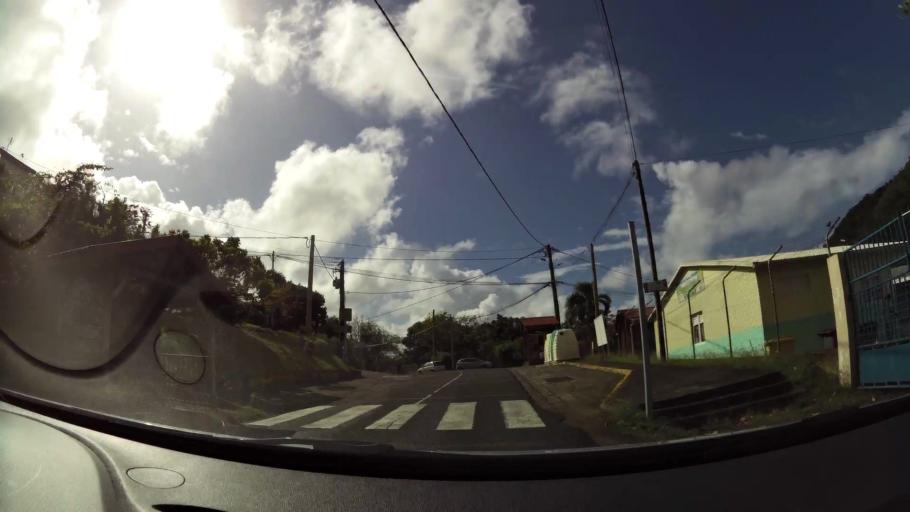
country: MQ
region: Martinique
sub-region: Martinique
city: Les Trois-Ilets
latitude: 14.5247
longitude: -61.0756
